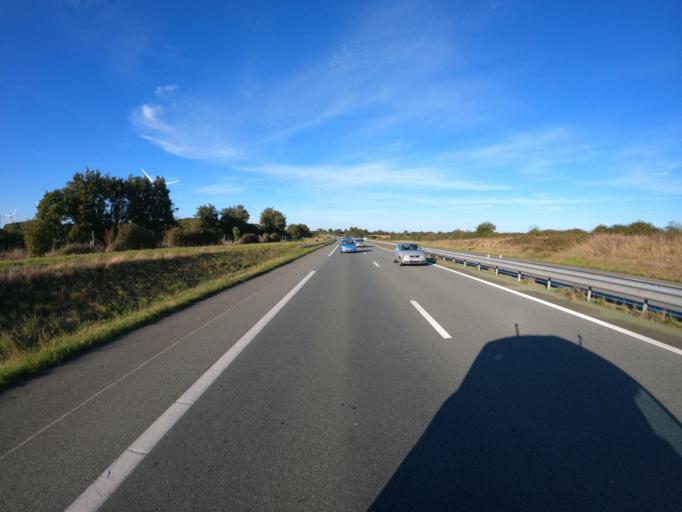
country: FR
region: Pays de la Loire
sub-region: Departement de Maine-et-Loire
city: Trementines
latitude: 47.1835
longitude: -0.7807
